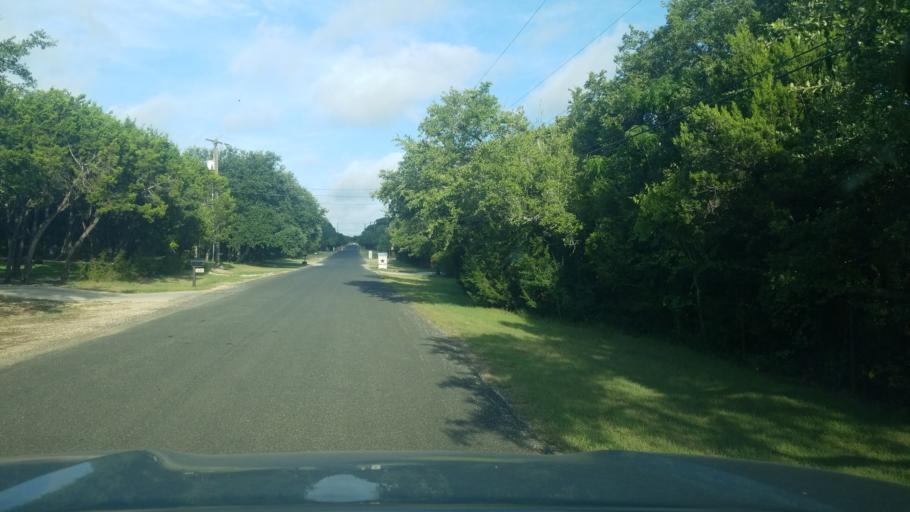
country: US
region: Texas
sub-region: Bexar County
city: Timberwood Park
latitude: 29.6951
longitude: -98.5166
